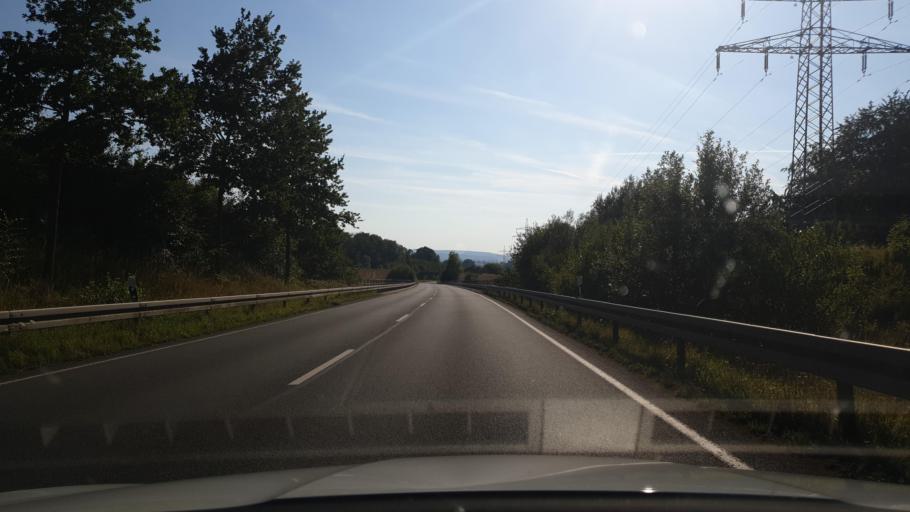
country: DE
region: North Rhine-Westphalia
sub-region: Regierungsbezirk Detmold
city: Lemgo
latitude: 51.9964
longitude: 8.9005
